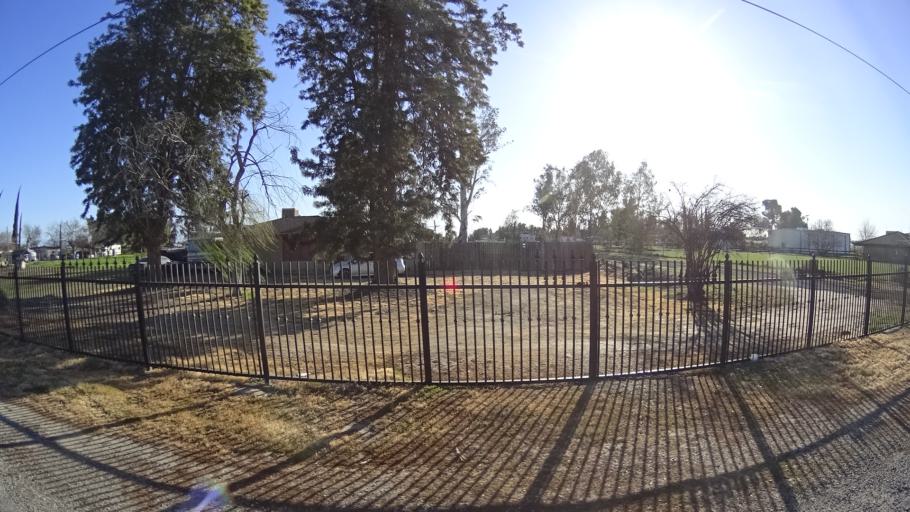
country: US
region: California
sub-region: Fresno County
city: West Park
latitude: 36.7809
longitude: -119.9163
